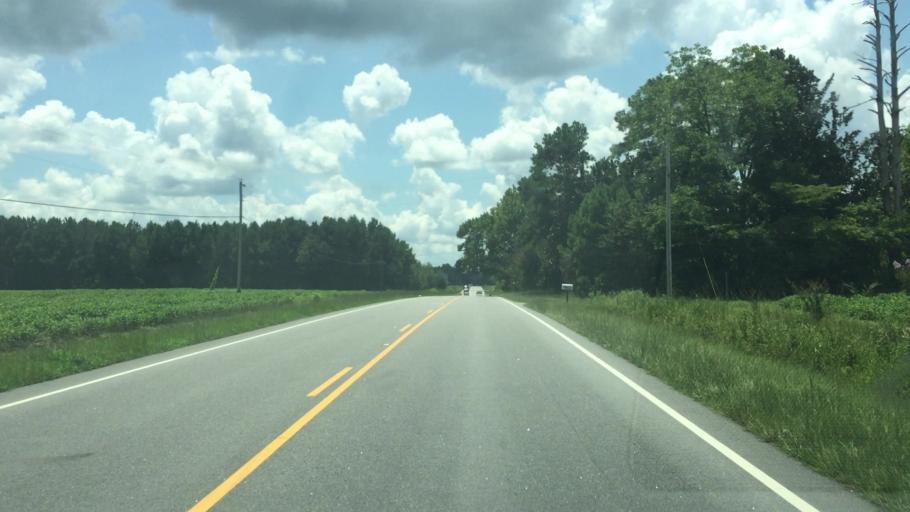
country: US
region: North Carolina
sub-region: Columbus County
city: Chadbourn
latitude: 34.2676
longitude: -78.8142
